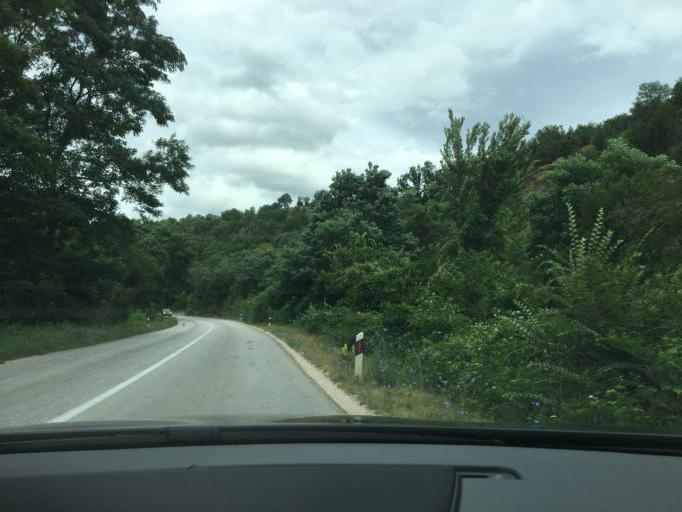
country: MK
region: Kriva Palanka
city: Kriva Palanka
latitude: 42.1767
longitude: 22.2402
